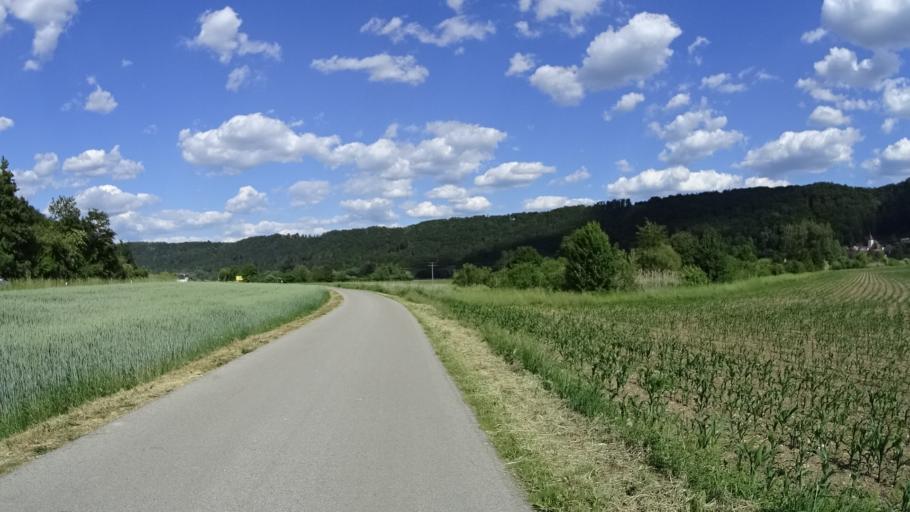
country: DE
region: Bavaria
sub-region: Upper Bavaria
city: Denkendorf
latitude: 48.9951
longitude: 11.4286
